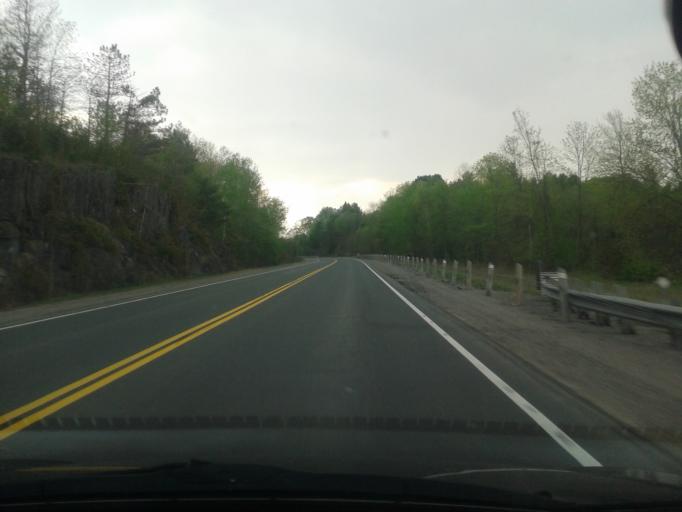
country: CA
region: Ontario
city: Belleville
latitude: 44.5403
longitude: -77.3644
